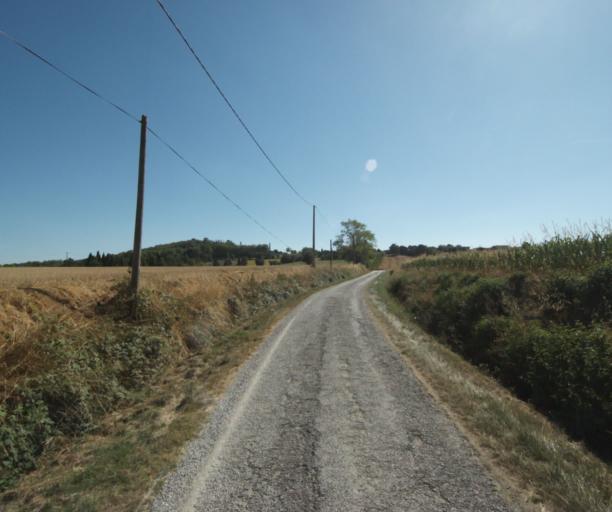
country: FR
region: Midi-Pyrenees
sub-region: Departement de la Haute-Garonne
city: Saint-Felix-Lauragais
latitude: 43.4998
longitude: 1.9003
